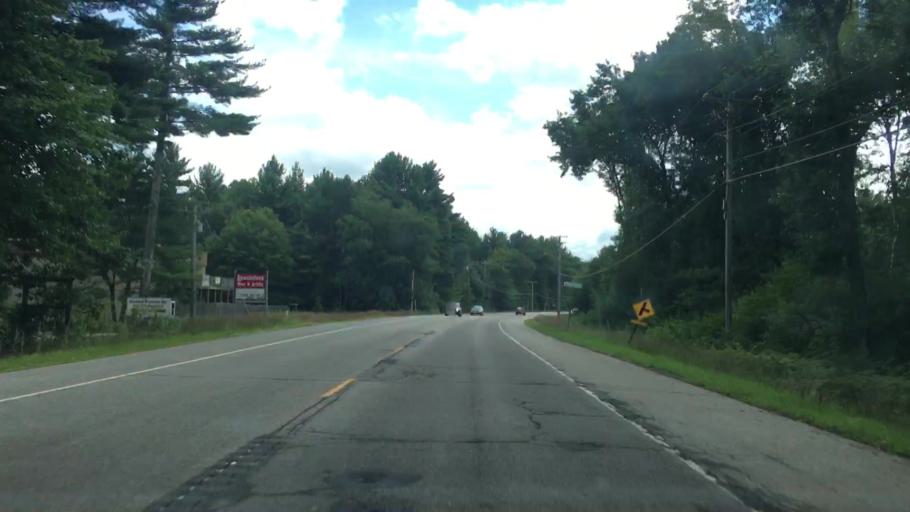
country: US
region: Maine
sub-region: York County
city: South Sanford
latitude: 43.4005
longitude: -70.7396
